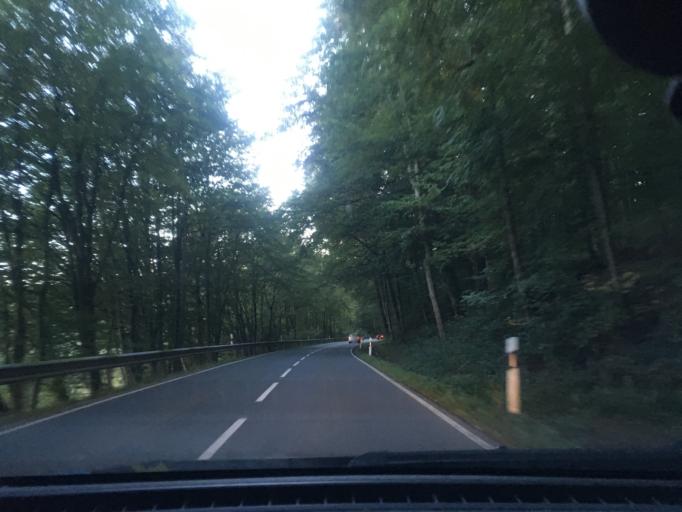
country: DE
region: Lower Saxony
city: Uslar
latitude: 51.6310
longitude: 9.6117
